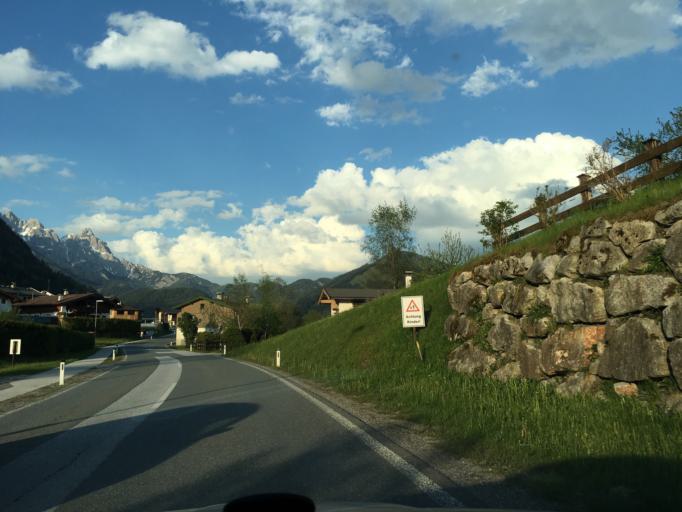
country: AT
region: Tyrol
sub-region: Politischer Bezirk Kitzbuhel
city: Fieberbrunn
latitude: 47.4976
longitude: 12.5522
